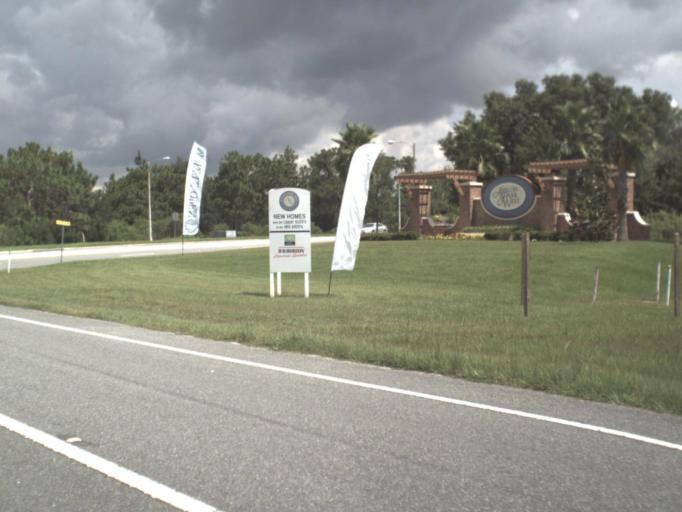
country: US
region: Florida
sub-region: Pasco County
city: Wesley Chapel
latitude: 28.2229
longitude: -82.2784
